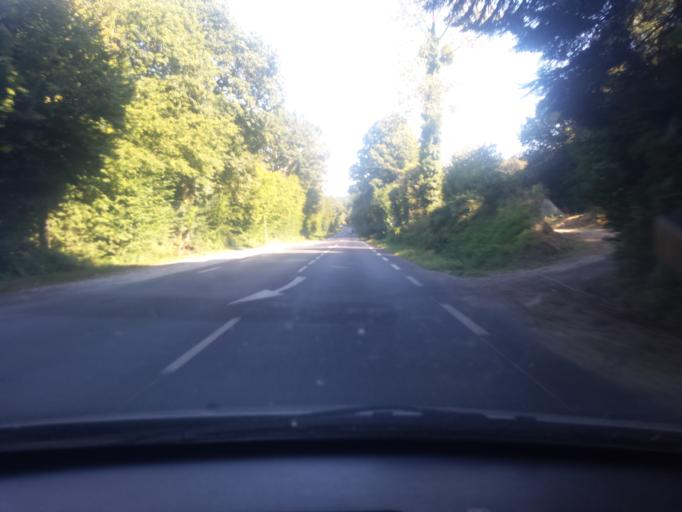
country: FR
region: Brittany
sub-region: Departement du Morbihan
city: Malguenac
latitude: 48.0983
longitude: -3.0542
